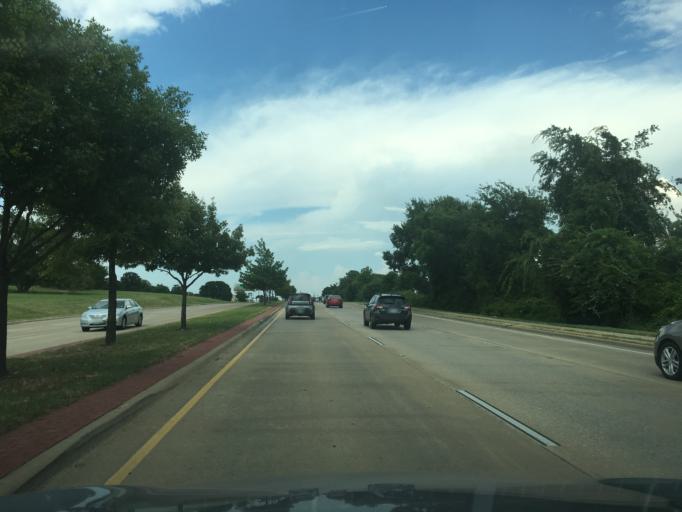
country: US
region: Texas
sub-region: Denton County
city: Denton
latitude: 33.2314
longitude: -97.1221
